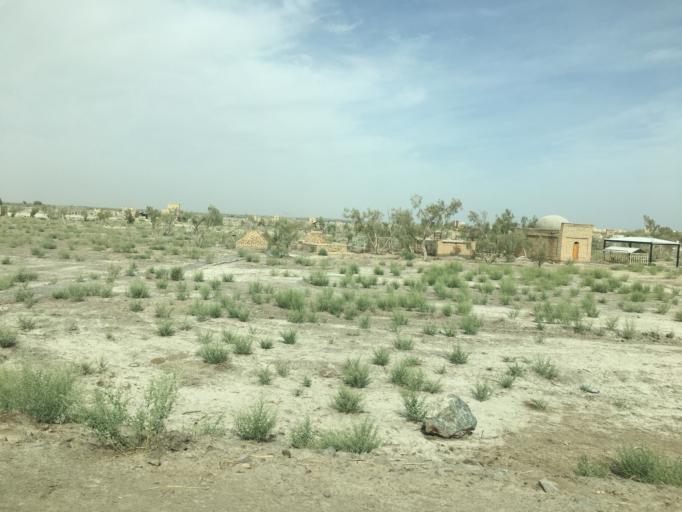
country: TM
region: Dasoguz
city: Tagta
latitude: 41.5657
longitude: 59.8158
